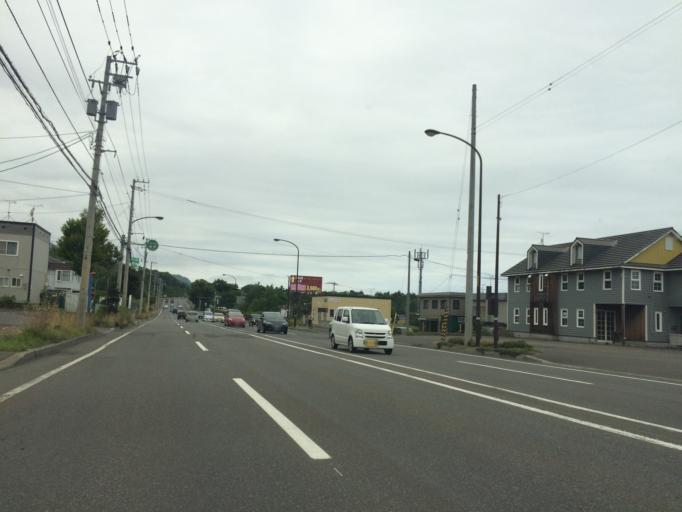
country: JP
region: Hokkaido
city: Otaru
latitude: 43.1442
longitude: 141.1445
